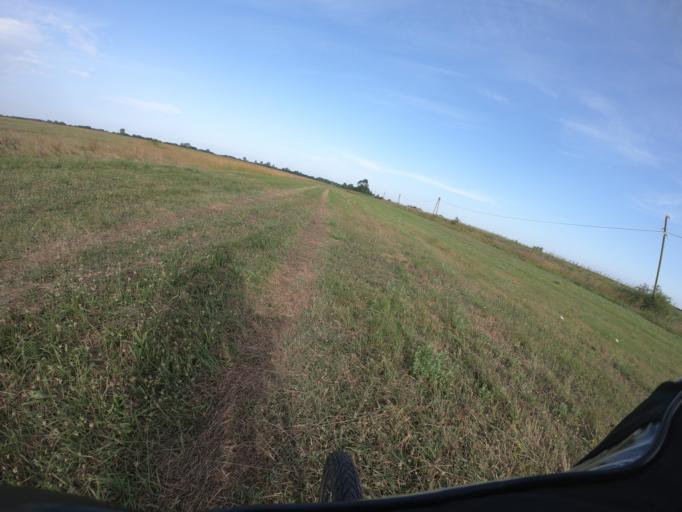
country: HU
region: Hajdu-Bihar
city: Tiszacsege
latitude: 47.6127
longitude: 21.0288
